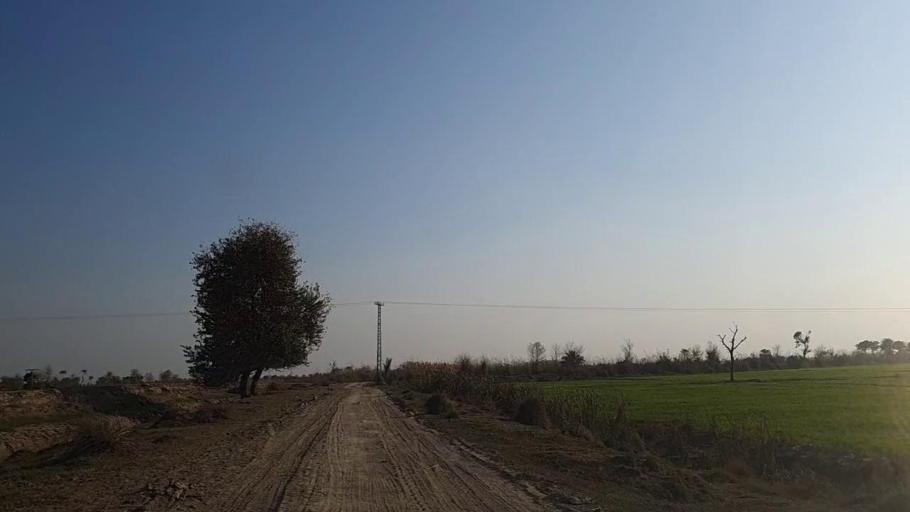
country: PK
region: Sindh
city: Daur
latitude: 26.4364
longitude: 68.3523
